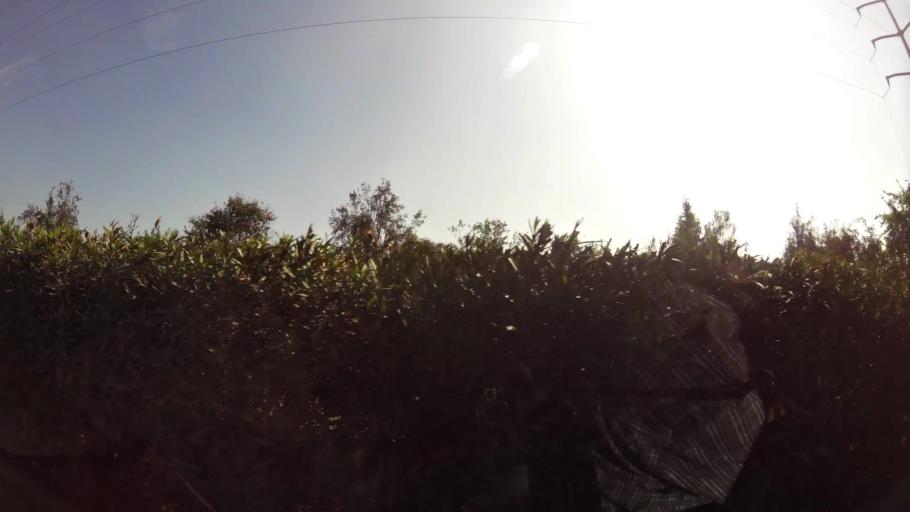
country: CL
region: Santiago Metropolitan
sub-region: Provincia de Santiago
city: Villa Presidente Frei, Nunoa, Santiago, Chile
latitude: -33.4097
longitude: -70.5139
